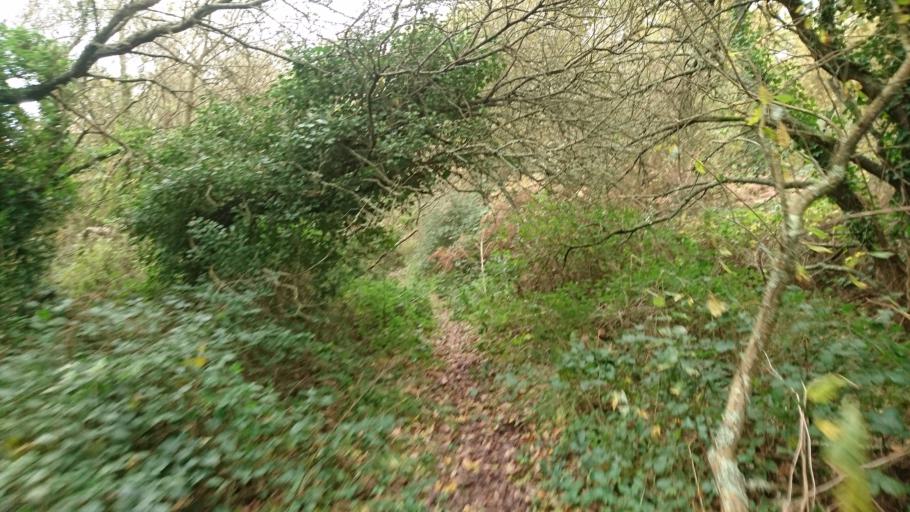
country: FR
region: Brittany
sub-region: Departement du Finistere
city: Lampaul-Plouarzel
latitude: 48.4371
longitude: -4.7690
